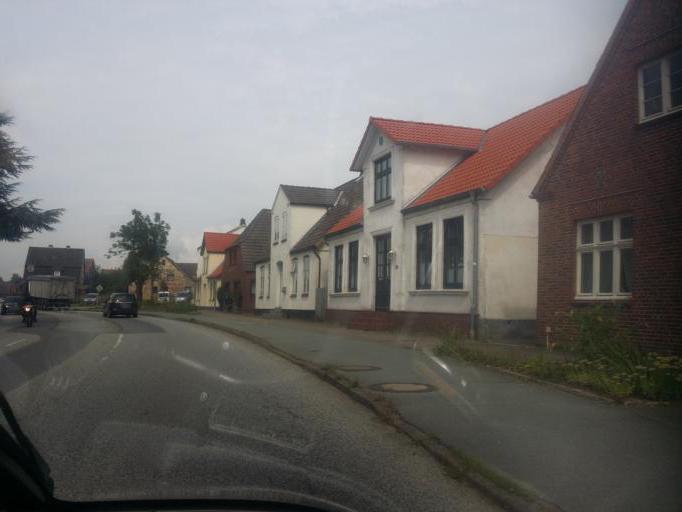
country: DE
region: Schleswig-Holstein
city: Meldorf
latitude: 54.0870
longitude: 9.0690
